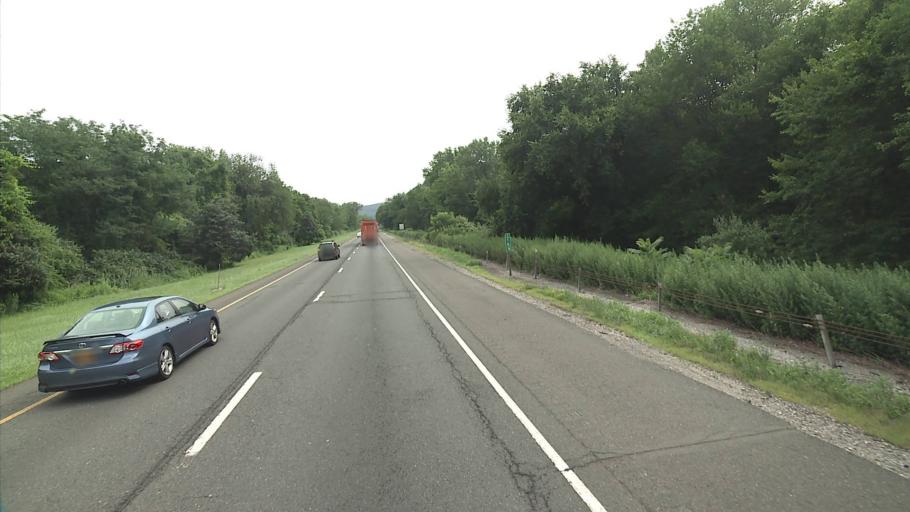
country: US
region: Connecticut
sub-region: Fairfield County
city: Newtown
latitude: 41.4184
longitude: -73.2620
